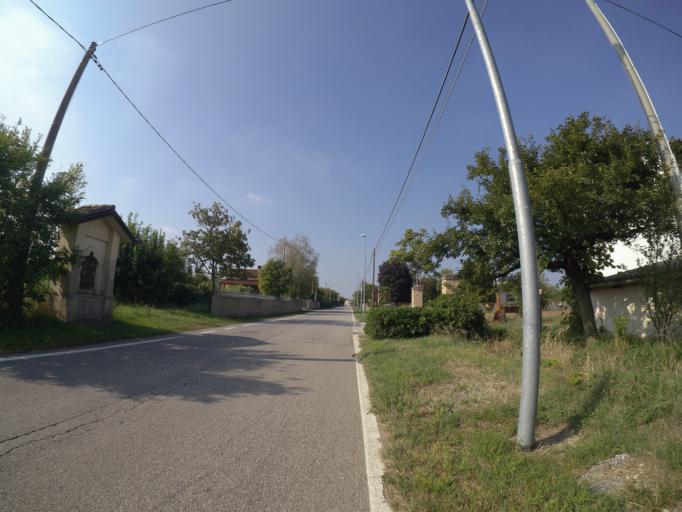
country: IT
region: Friuli Venezia Giulia
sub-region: Provincia di Udine
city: Basiliano
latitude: 45.9914
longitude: 13.0301
